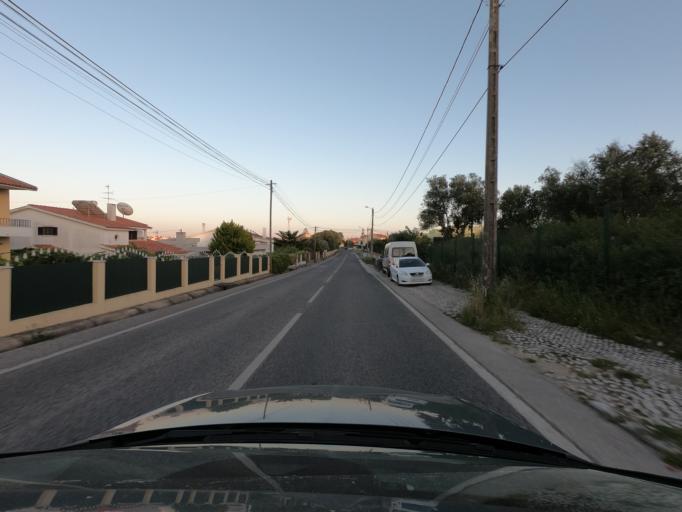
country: PT
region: Lisbon
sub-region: Sintra
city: Rio de Mouro
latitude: 38.7608
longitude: -9.3485
